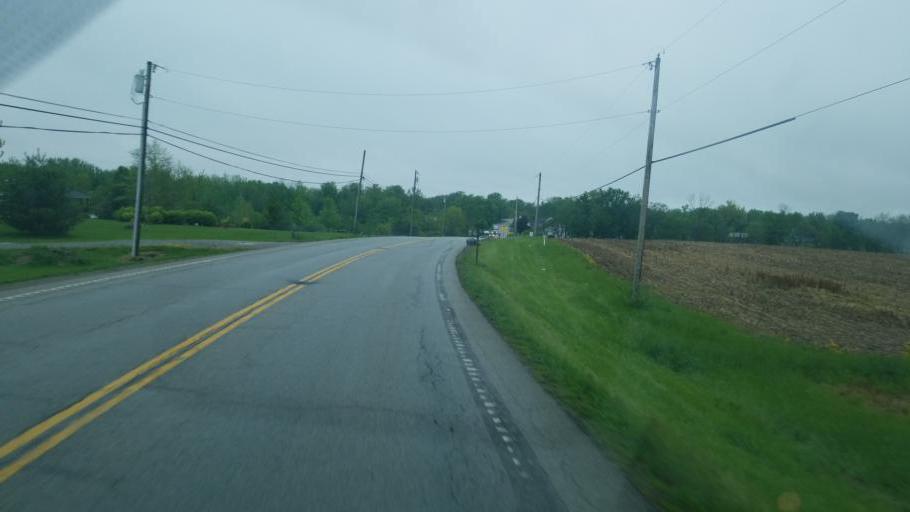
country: US
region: Ohio
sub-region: Highland County
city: Leesburg
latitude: 39.2801
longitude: -83.5940
